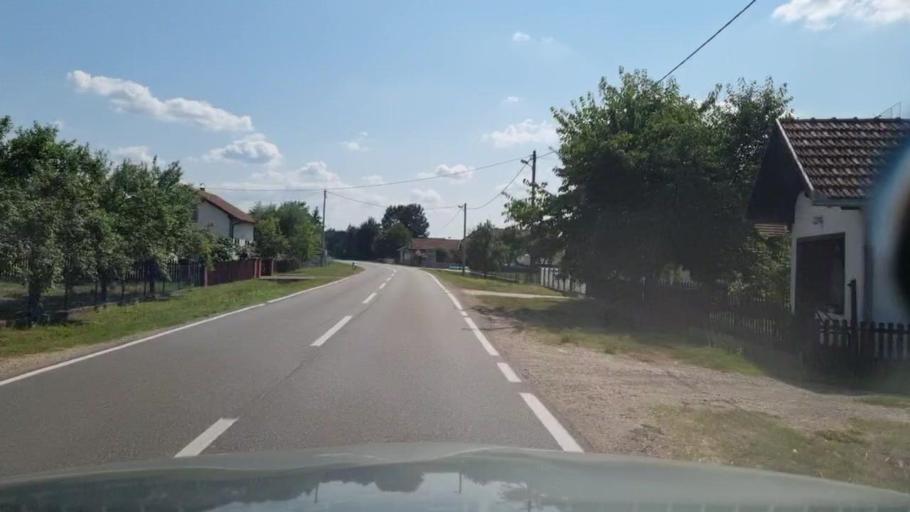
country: BA
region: Federation of Bosnia and Herzegovina
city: Odzak
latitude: 45.0346
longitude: 18.3654
